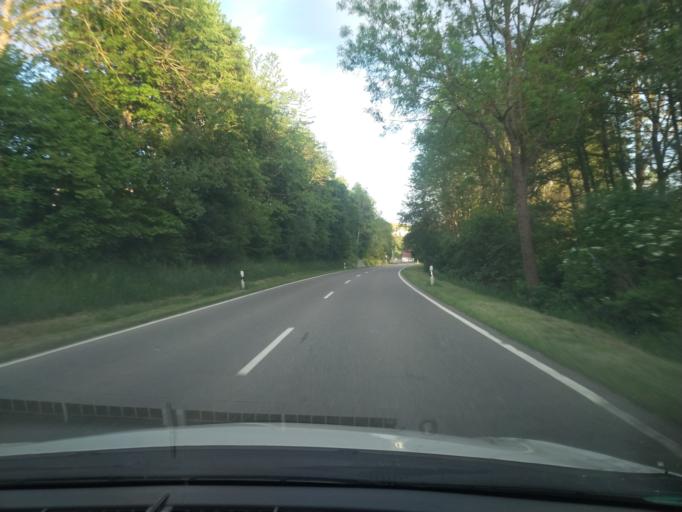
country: DE
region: Baden-Wuerttemberg
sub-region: Freiburg Region
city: Bonndorf im Schwarzwald
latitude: 47.8011
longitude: 8.3481
